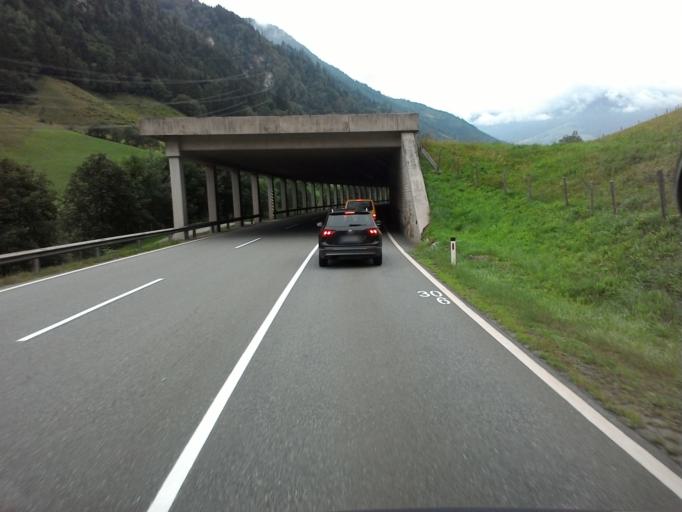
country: AT
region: Salzburg
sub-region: Politischer Bezirk Zell am See
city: Mittersill
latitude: 47.2370
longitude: 12.4925
